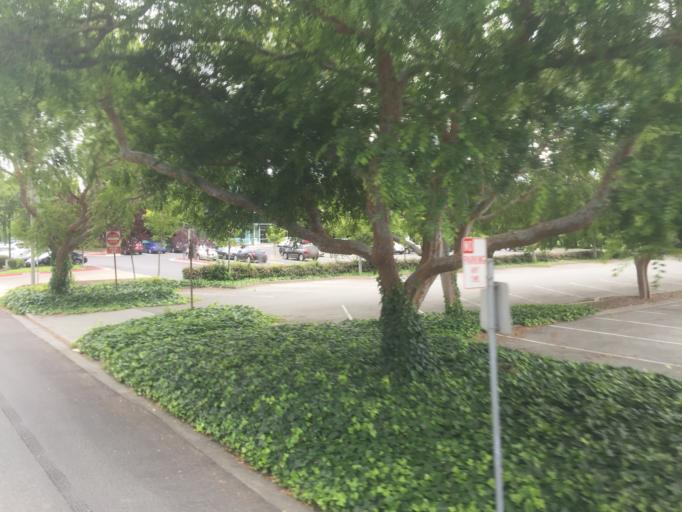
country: US
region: California
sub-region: Santa Clara County
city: Sunnyvale
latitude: 37.3953
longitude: -122.0414
